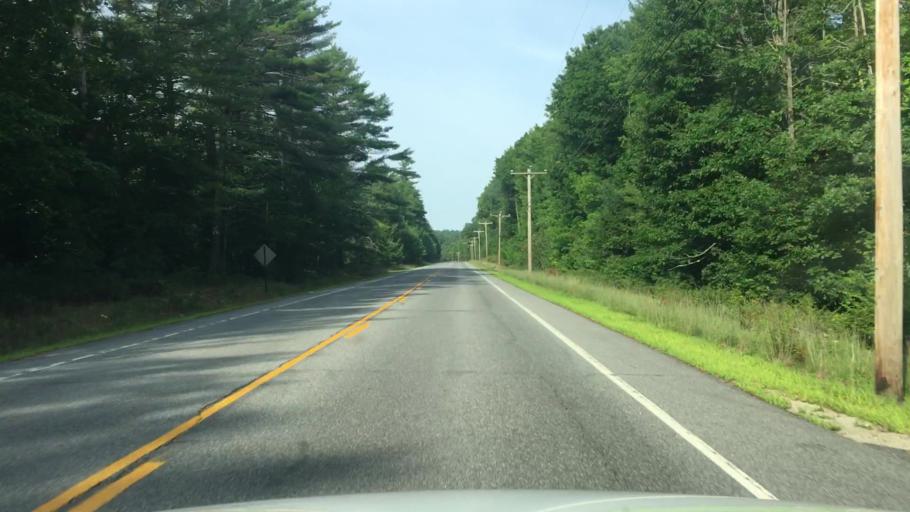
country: US
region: Maine
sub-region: York County
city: Cornish
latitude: 43.8056
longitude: -70.8439
